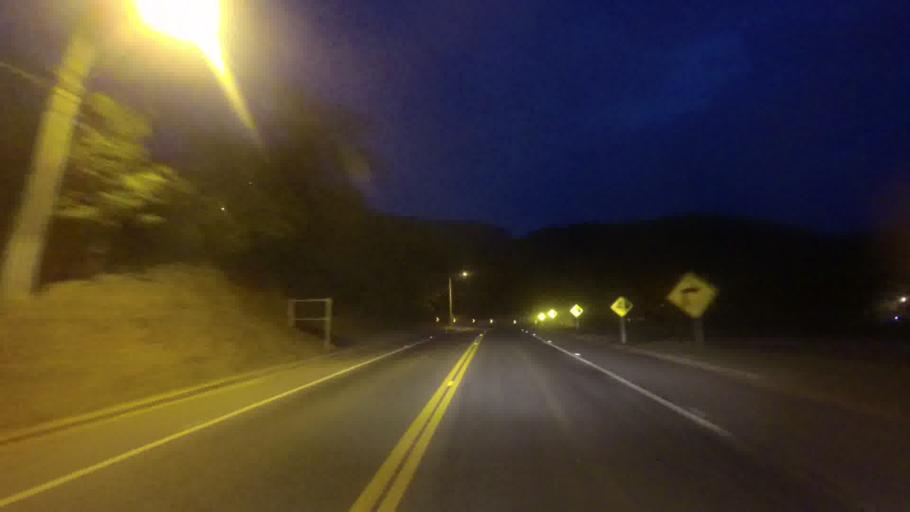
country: BR
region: Rio de Janeiro
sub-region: Sapucaia
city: Sapucaia
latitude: -21.9884
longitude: -42.9025
